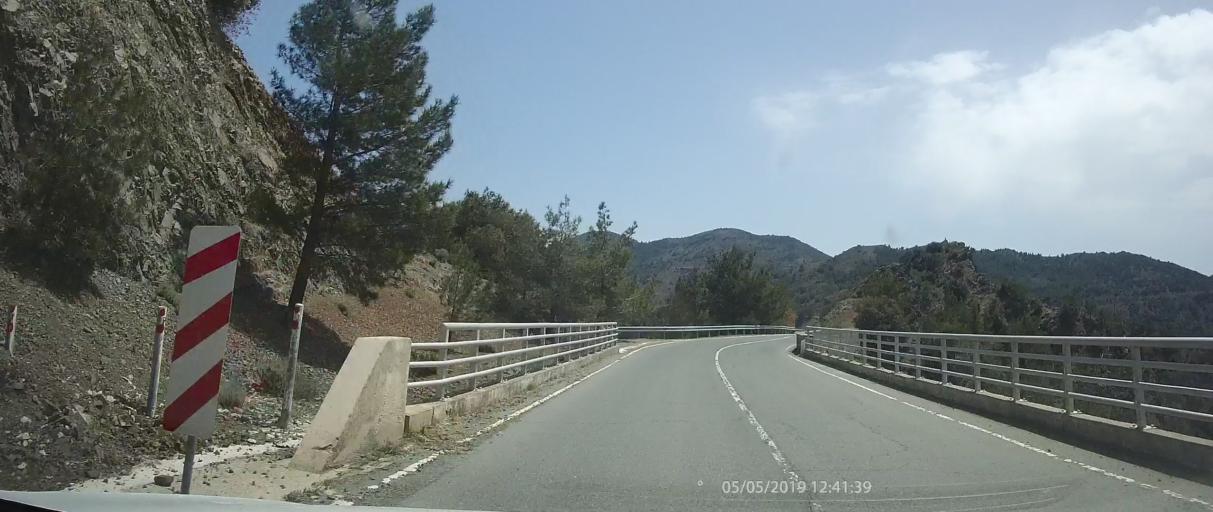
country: CY
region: Lefkosia
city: Kakopetria
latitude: 34.9806
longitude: 32.8092
